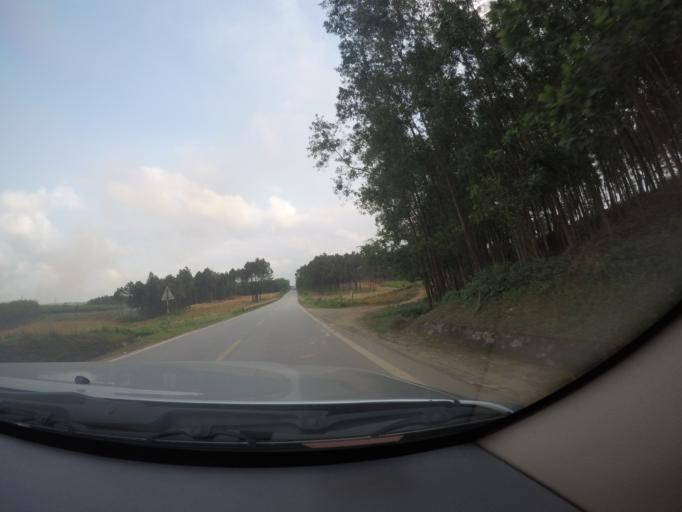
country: VN
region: Quang Binh
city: Kien Giang
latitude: 17.1179
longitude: 106.8290
